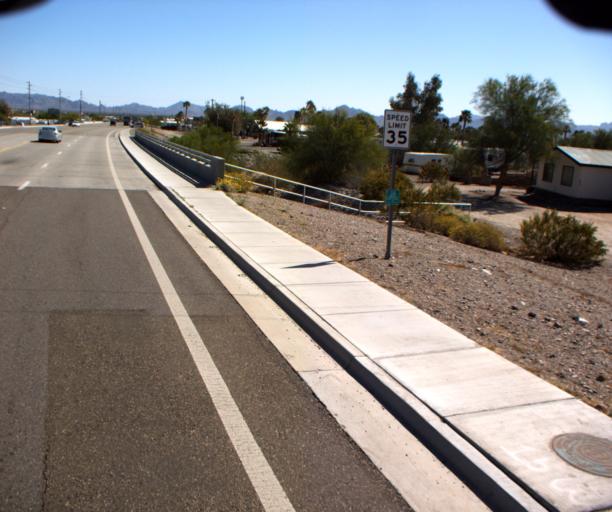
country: US
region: Arizona
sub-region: La Paz County
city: Quartzsite
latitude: 33.6655
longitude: -114.2251
